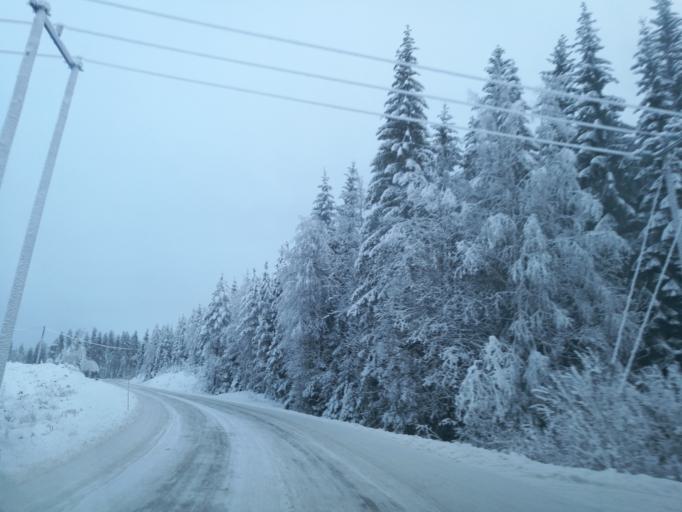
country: NO
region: Hedmark
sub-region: Grue
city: Kirkenaer
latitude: 60.4484
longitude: 12.4690
